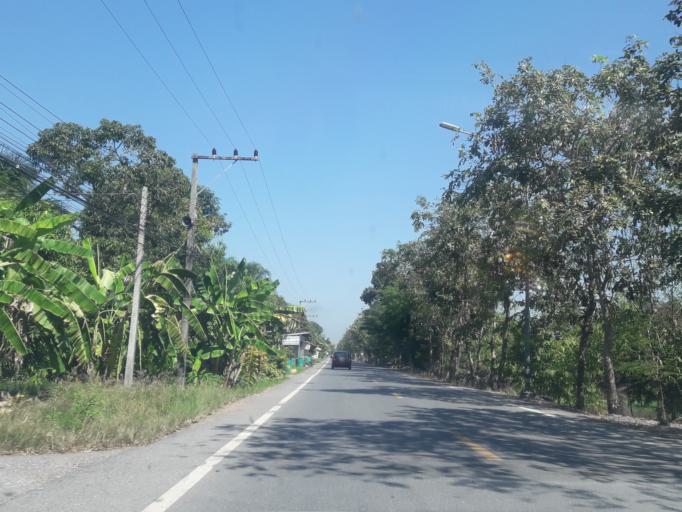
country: TH
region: Pathum Thani
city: Nong Suea
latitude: 14.1751
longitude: 100.8458
